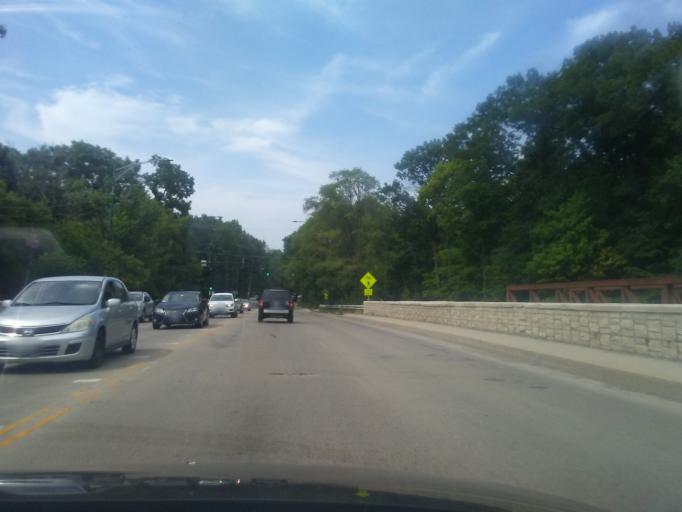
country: US
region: Illinois
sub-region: Cook County
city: Lincolnwood
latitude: 41.9900
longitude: -87.7661
